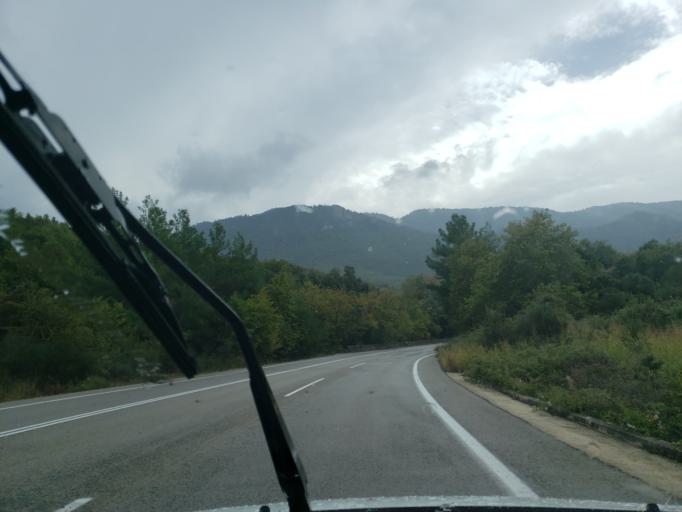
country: GR
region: Central Greece
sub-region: Nomos Fthiotidos
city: Anthili
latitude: 38.7892
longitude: 22.4943
